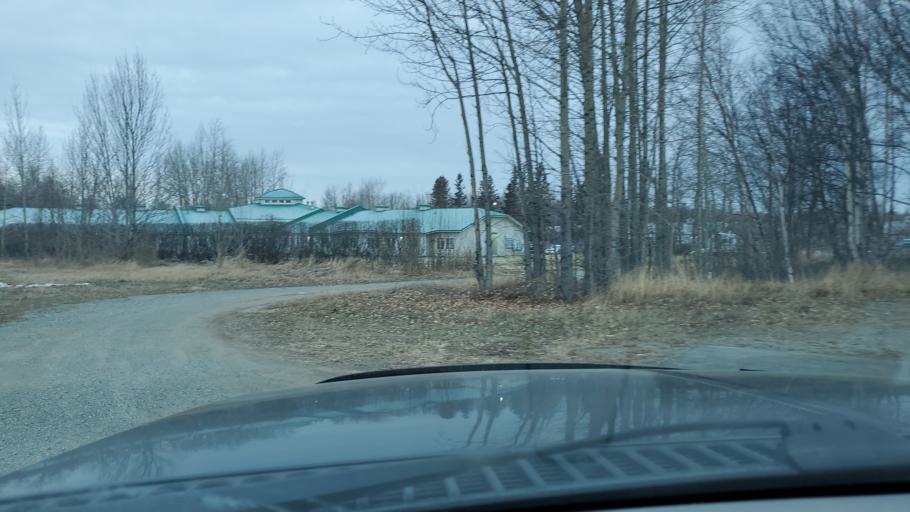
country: US
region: Alaska
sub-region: Matanuska-Susitna Borough
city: Palmer
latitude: 61.5969
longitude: -149.1078
